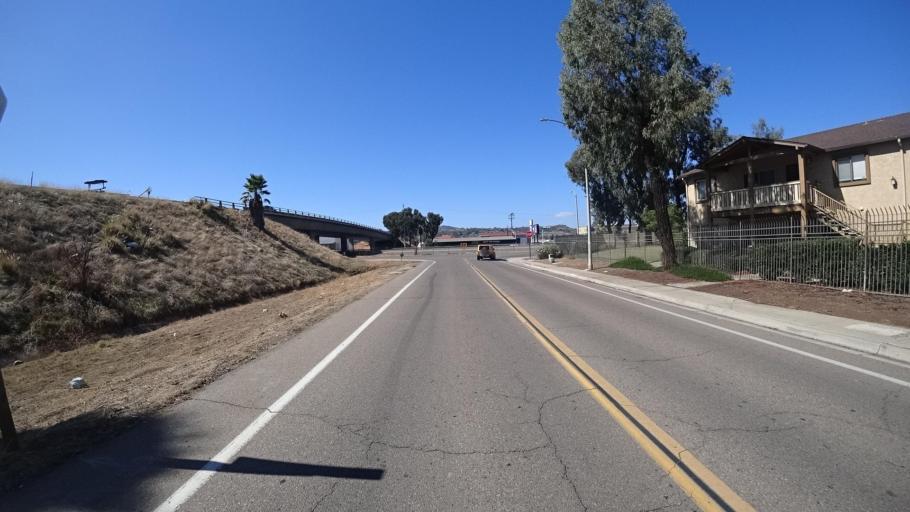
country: US
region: California
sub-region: San Diego County
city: El Cajon
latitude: 32.8136
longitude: -116.9607
